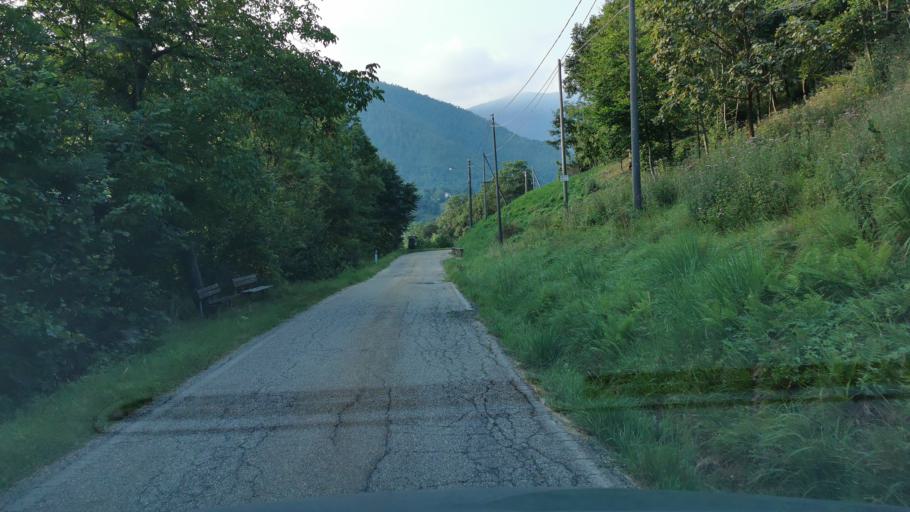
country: IT
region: Piedmont
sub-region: Provincia di Torino
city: La Villa
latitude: 45.2602
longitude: 7.4325
